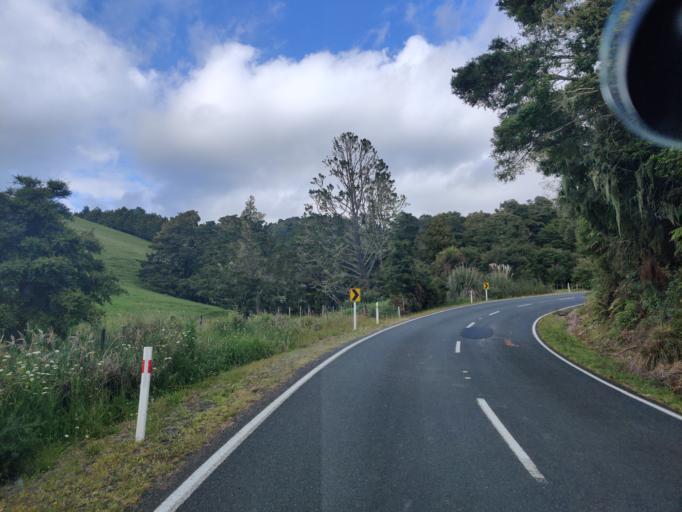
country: NZ
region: Northland
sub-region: Whangarei
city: Ngunguru
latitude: -35.5786
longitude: 174.4161
